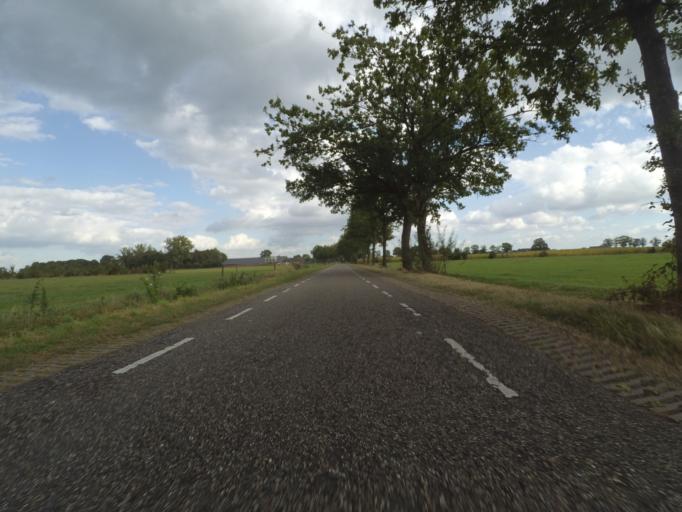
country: NL
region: Utrecht
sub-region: Gemeente Utrechtse Heuvelrug
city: Overberg
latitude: 52.0658
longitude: 5.5177
